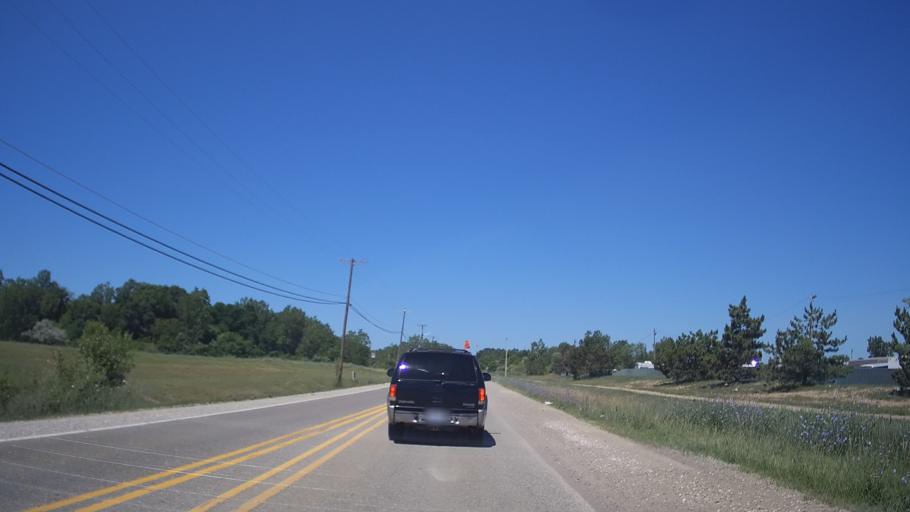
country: US
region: Michigan
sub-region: Macomb County
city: Shelby
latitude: 42.6514
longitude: -83.0771
